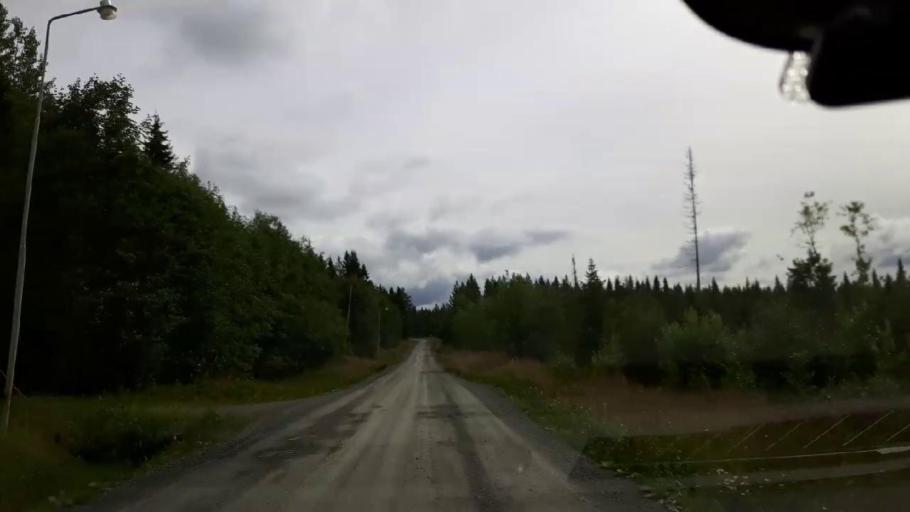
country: SE
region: Jaemtland
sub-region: Krokoms Kommun
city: Valla
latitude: 63.6430
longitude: 13.9940
